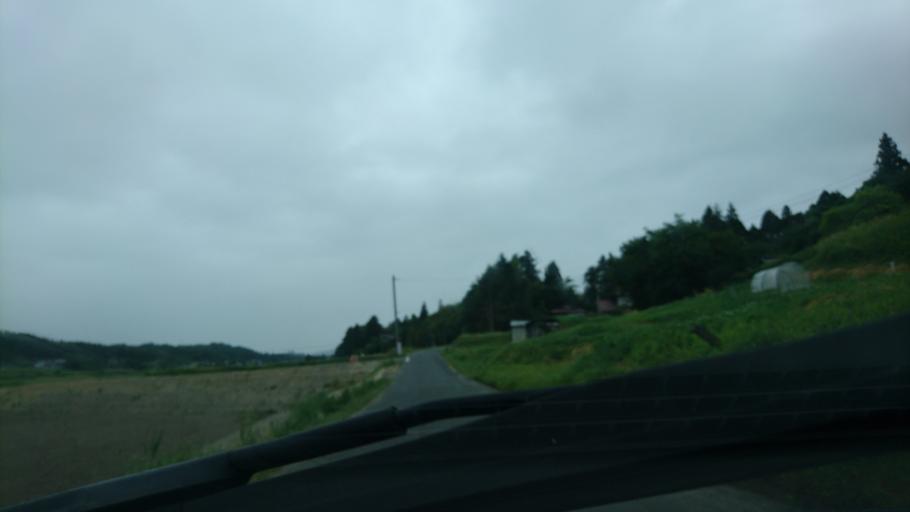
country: JP
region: Iwate
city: Ichinoseki
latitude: 38.9145
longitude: 141.1791
